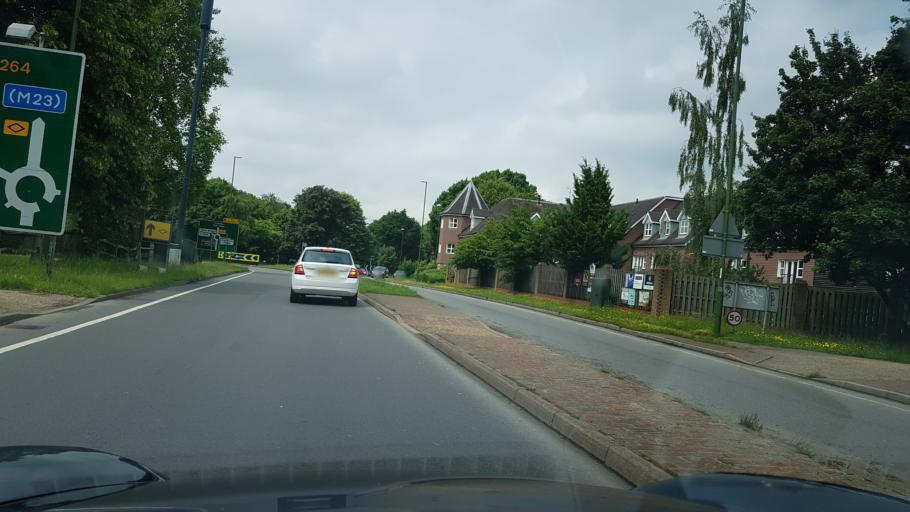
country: GB
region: England
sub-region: West Sussex
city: Copthorne
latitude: 51.1337
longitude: -0.1242
